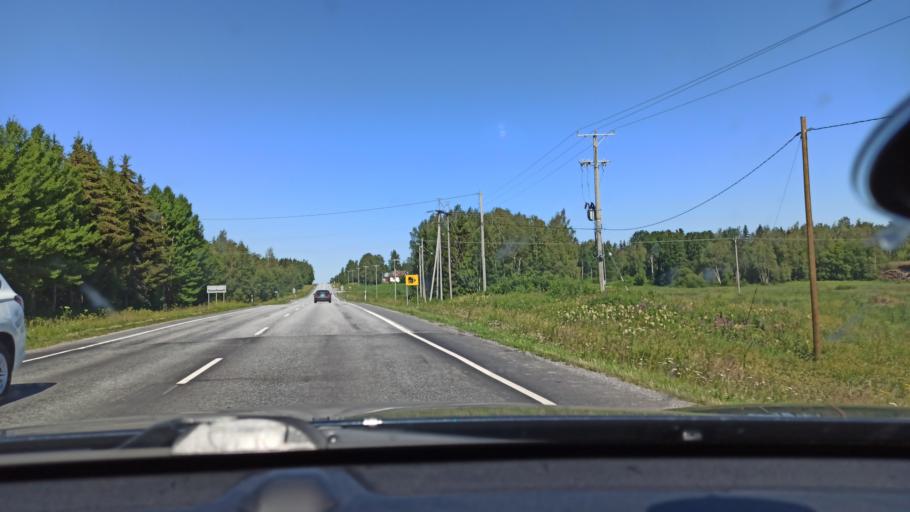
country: FI
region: Ostrobothnia
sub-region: Vaasa
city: Voera
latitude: 63.2388
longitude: 22.2586
